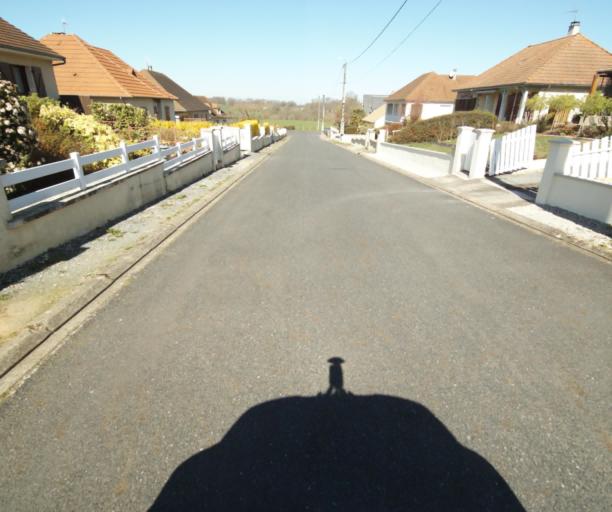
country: FR
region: Limousin
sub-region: Departement de la Correze
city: Seilhac
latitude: 45.3701
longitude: 1.7174
